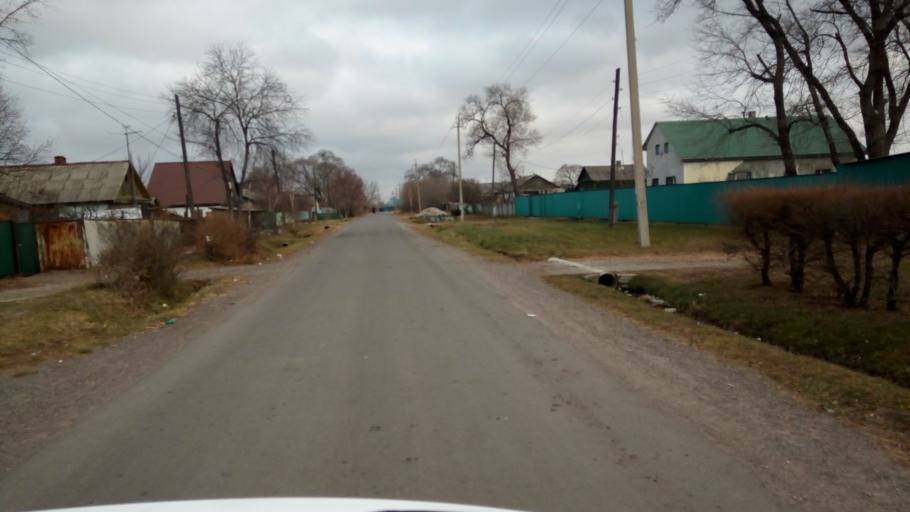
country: RU
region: Primorskiy
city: Ussuriysk
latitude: 43.7985
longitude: 131.9513
